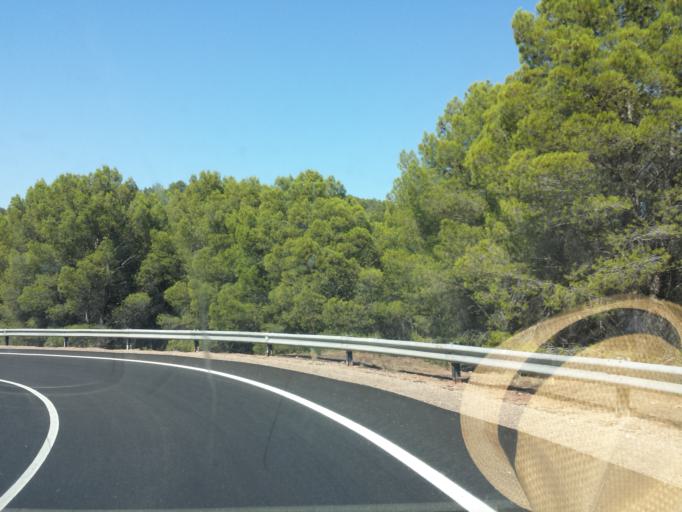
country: ES
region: Aragon
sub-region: Provincia de Zaragoza
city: Nuevalos
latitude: 41.2125
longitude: -1.7623
